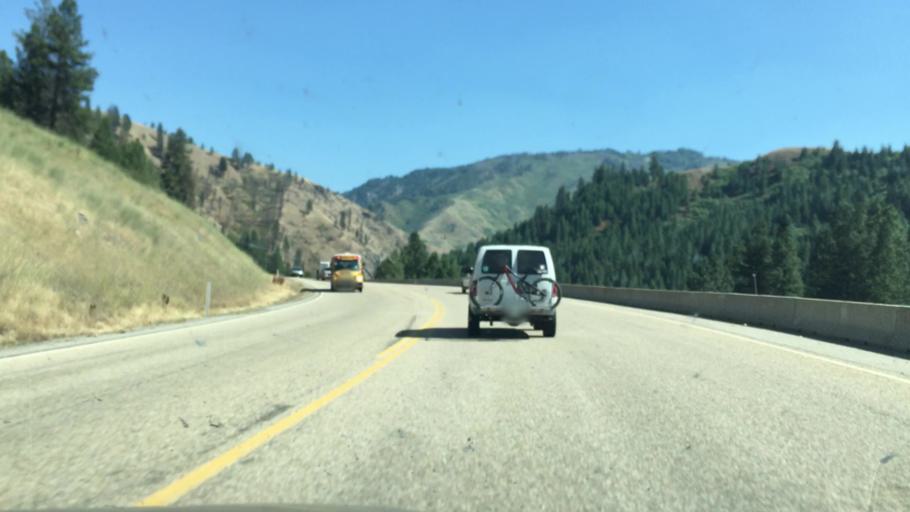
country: US
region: Idaho
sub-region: Boise County
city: Idaho City
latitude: 44.1136
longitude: -116.1051
